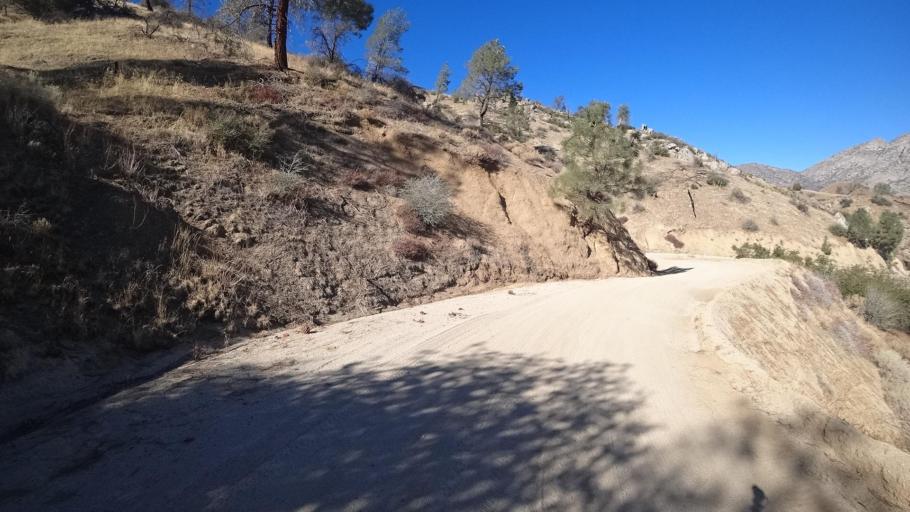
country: US
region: California
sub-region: Kern County
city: Wofford Heights
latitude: 35.7034
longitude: -118.4895
